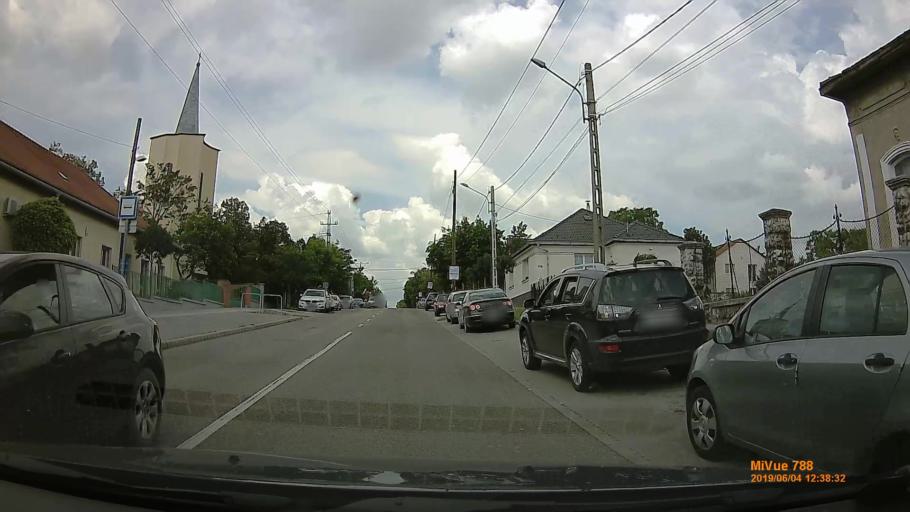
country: HU
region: Budapest
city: Budapest XXII. keruelet
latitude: 47.4057
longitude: 18.9994
